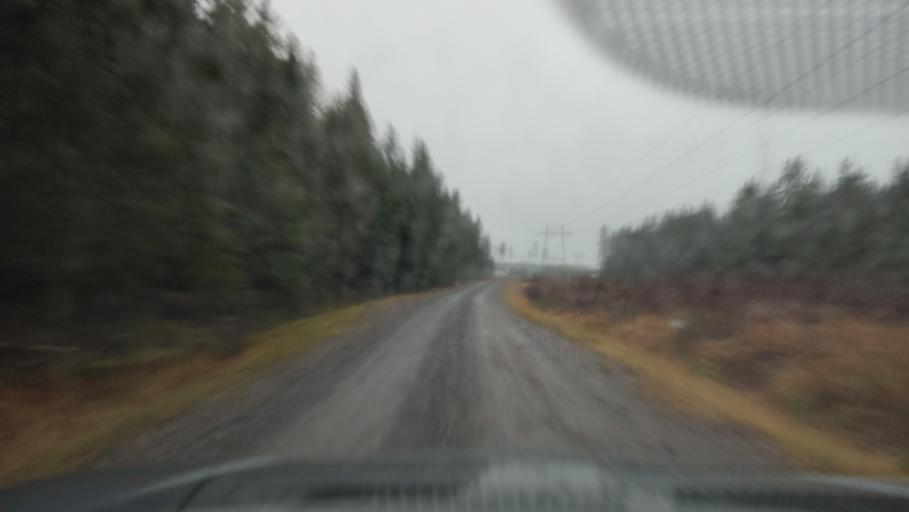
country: FI
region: Southern Ostrobothnia
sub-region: Suupohja
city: Karijoki
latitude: 62.2115
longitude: 21.7300
